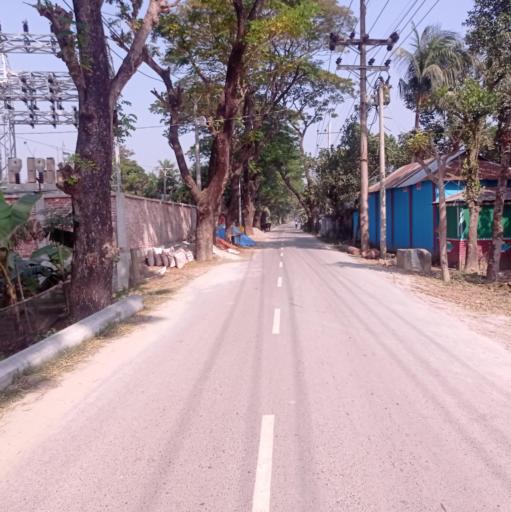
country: BD
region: Dhaka
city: Narsingdi
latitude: 24.0524
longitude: 90.6827
